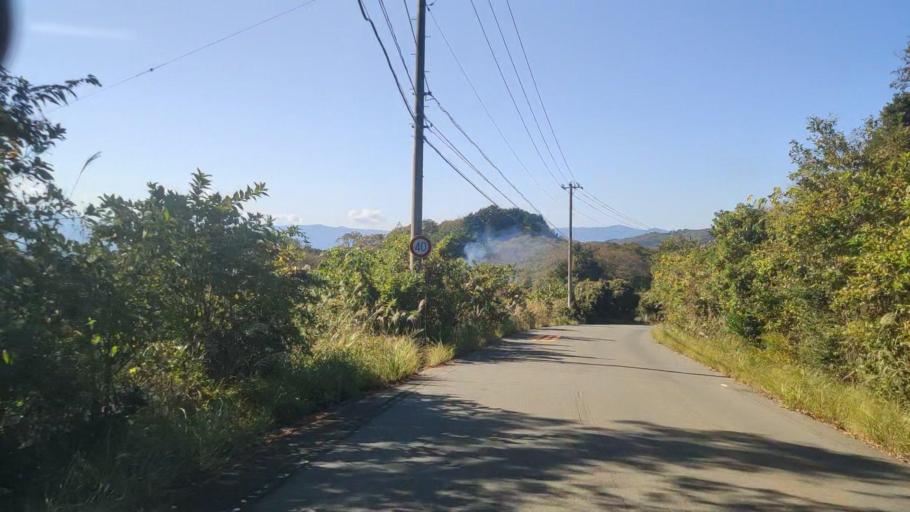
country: JP
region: Shizuoka
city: Atami
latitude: 35.0417
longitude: 139.0215
